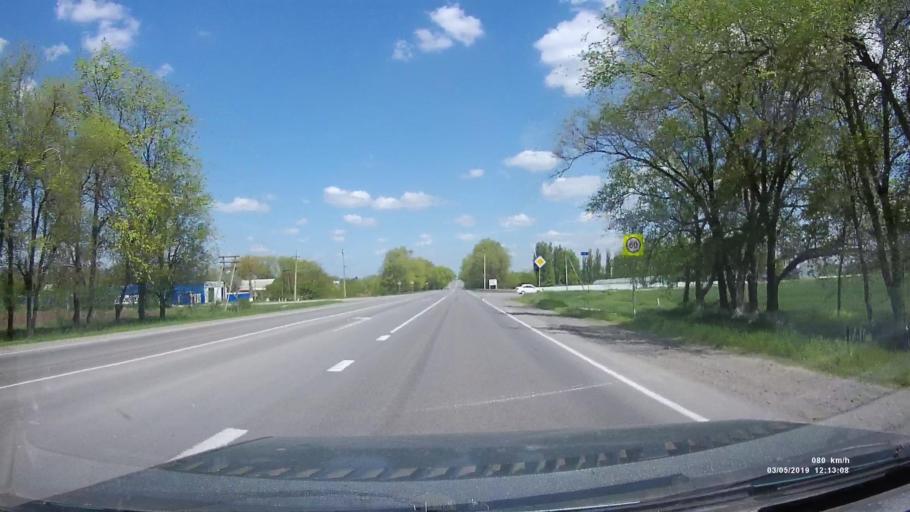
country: RU
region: Rostov
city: Bagayevskaya
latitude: 47.3296
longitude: 40.5527
